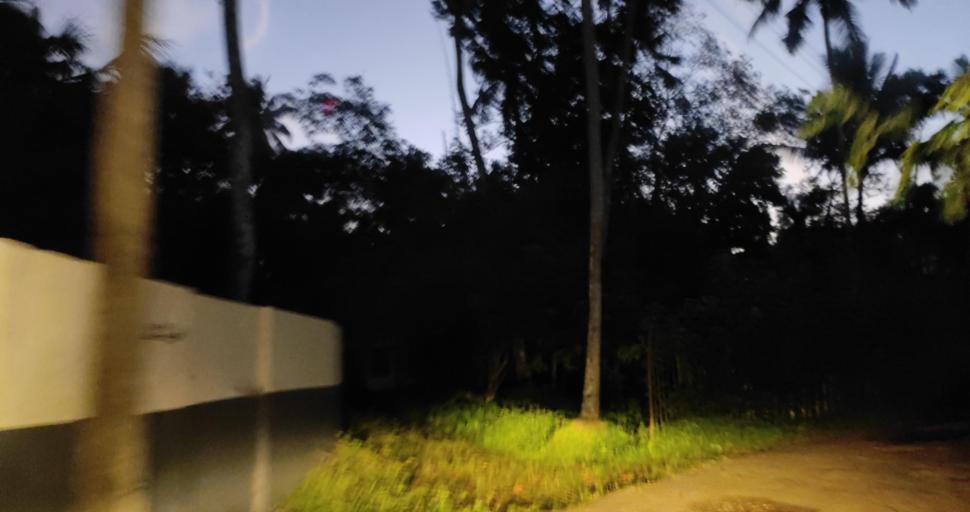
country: IN
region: Kerala
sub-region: Alappuzha
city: Shertallai
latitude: 9.6169
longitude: 76.3626
